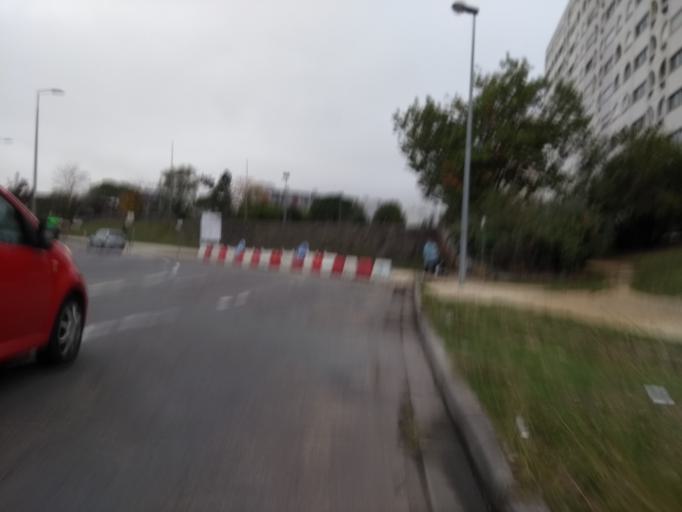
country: FR
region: Aquitaine
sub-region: Departement de la Gironde
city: Talence
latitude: 44.7895
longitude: -0.5871
